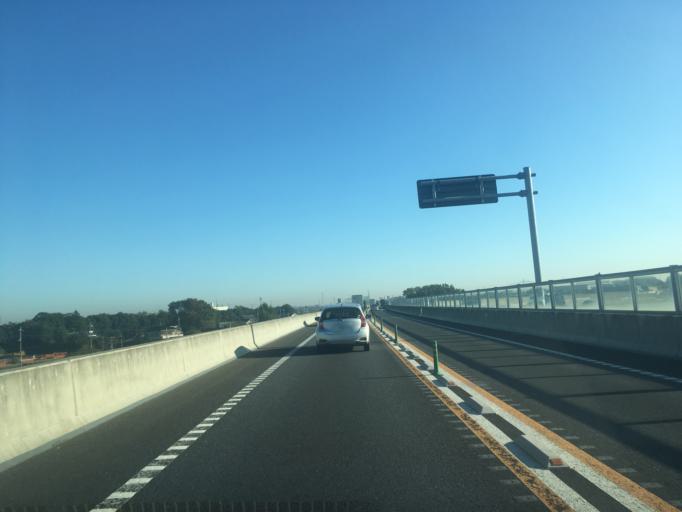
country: JP
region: Saitama
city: Kukichuo
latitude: 36.0537
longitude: 139.6896
